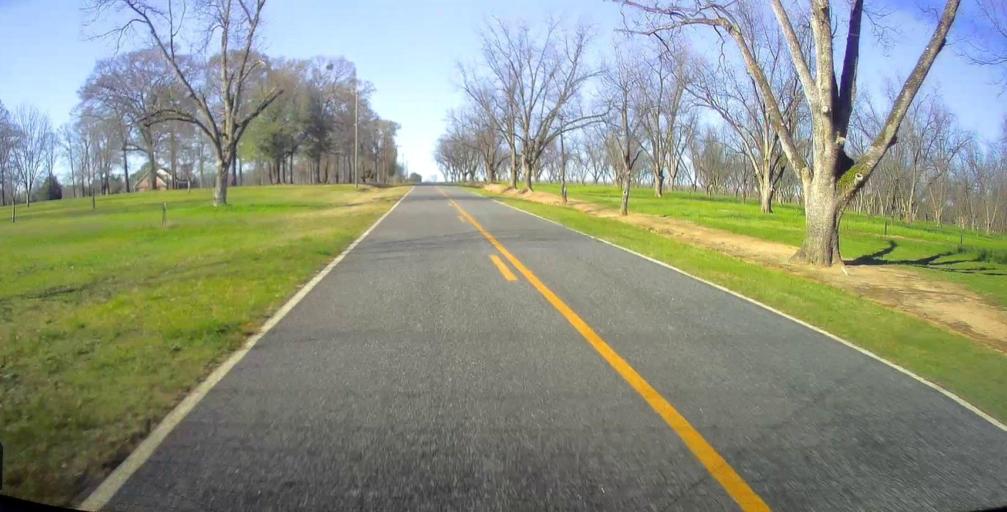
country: US
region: Georgia
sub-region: Peach County
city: Fort Valley
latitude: 32.5996
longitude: -83.8524
